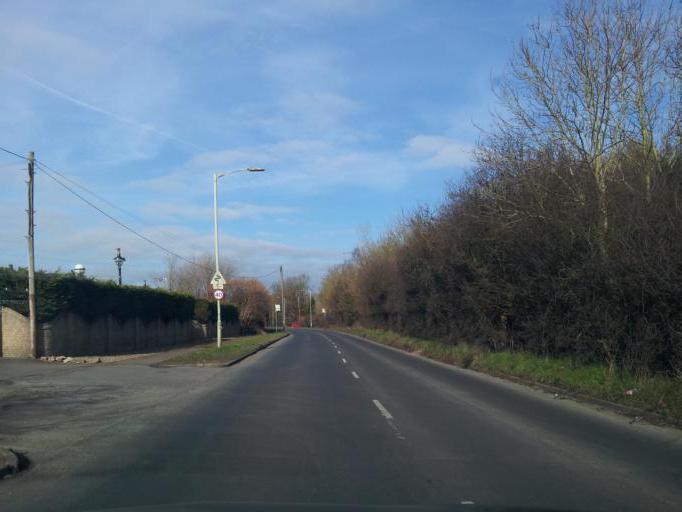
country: GB
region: England
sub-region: Hertfordshire
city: Hatfield
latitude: 51.7430
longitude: -0.2710
